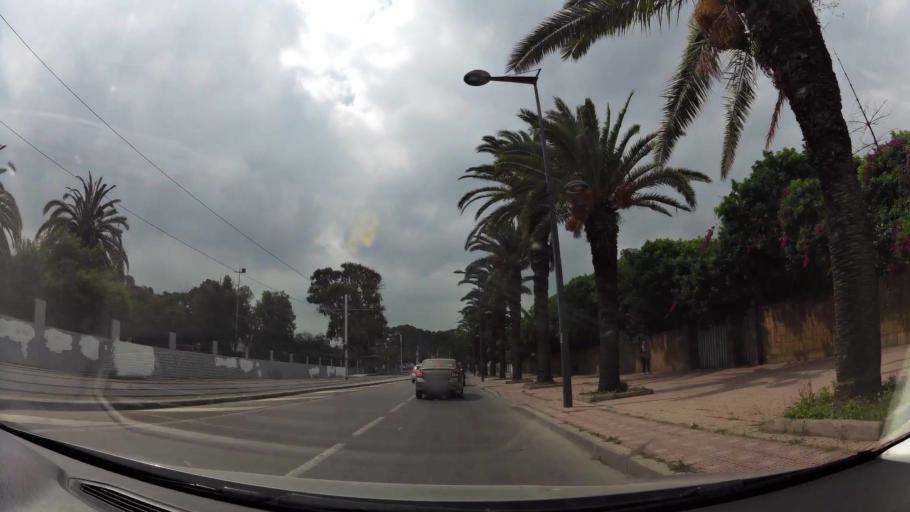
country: MA
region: Rabat-Sale-Zemmour-Zaer
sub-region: Rabat
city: Rabat
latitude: 34.0055
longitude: -6.8437
